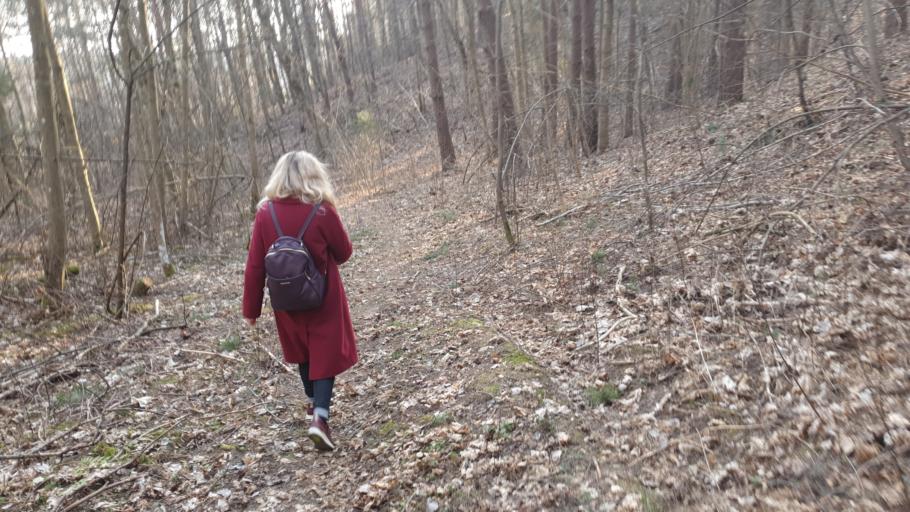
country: LT
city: Nemencine
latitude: 54.8728
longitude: 25.5711
